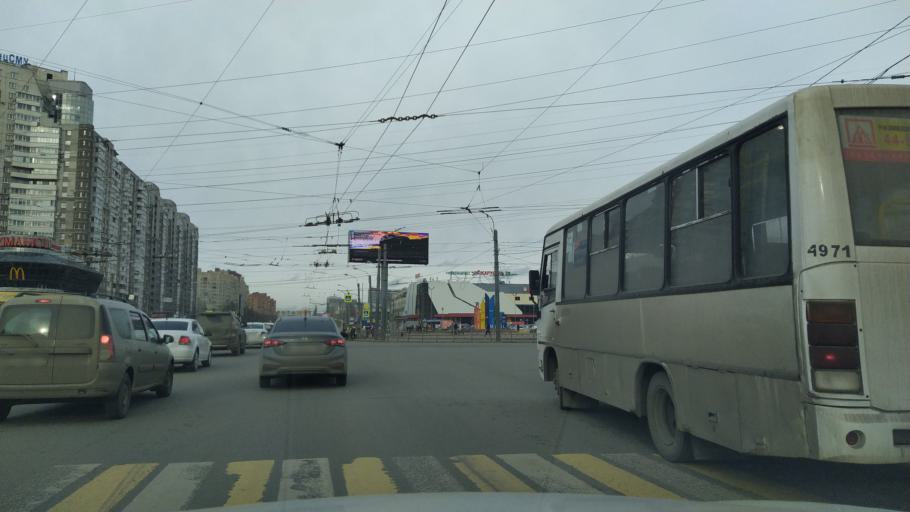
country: RU
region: Leningrad
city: Chernaya Rechka
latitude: 60.0026
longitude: 30.2984
